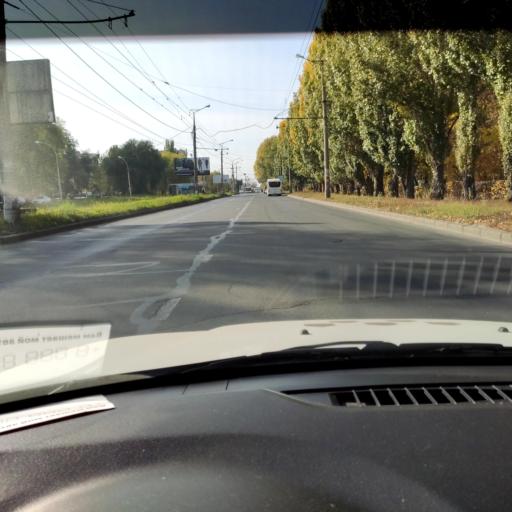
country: RU
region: Samara
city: Tol'yatti
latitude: 53.5105
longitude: 49.4340
